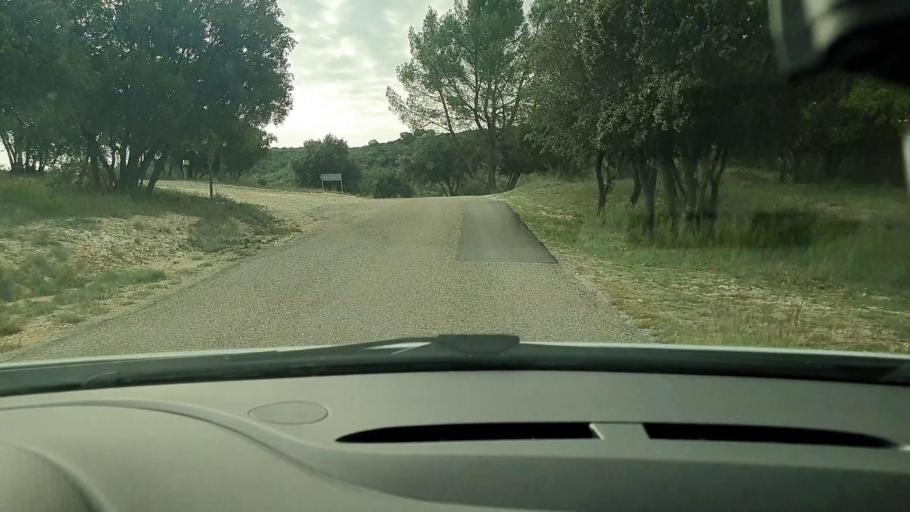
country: FR
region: Languedoc-Roussillon
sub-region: Departement du Gard
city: Montaren-et-Saint-Mediers
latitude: 44.0929
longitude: 4.3270
